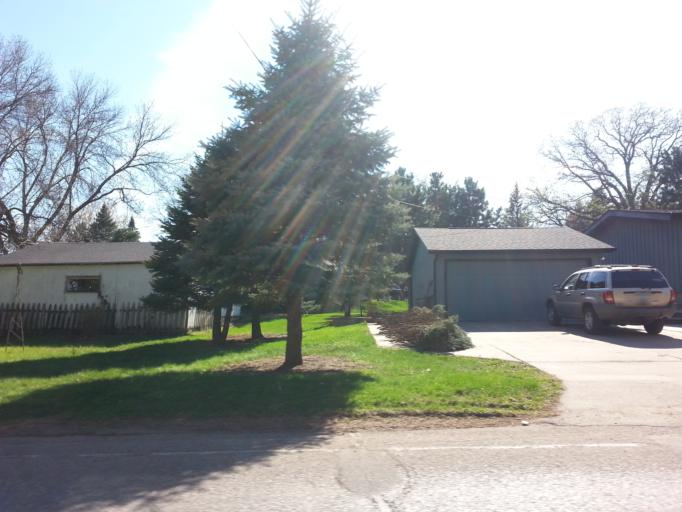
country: US
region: Minnesota
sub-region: Washington County
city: Oak Park Heights
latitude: 45.0389
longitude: -92.7993
